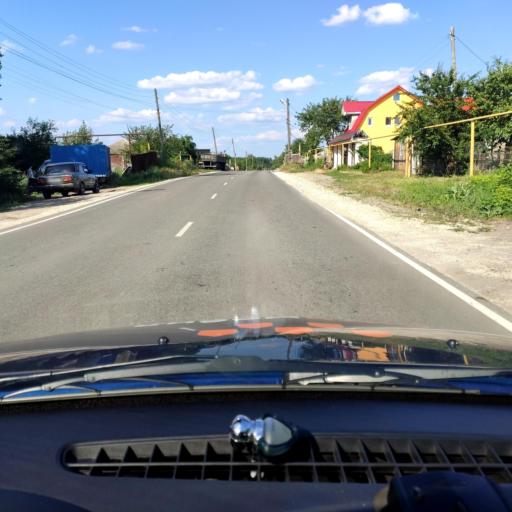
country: RU
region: Voronezj
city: Devitsa
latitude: 51.6474
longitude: 38.9678
